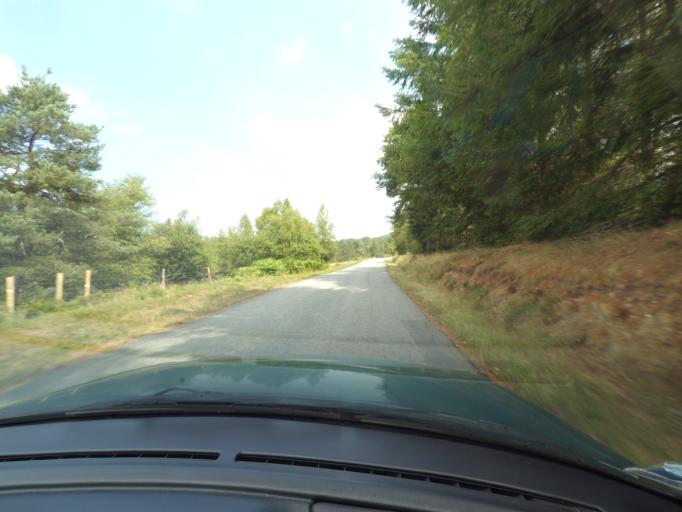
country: FR
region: Limousin
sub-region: Departement de la Correze
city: Bugeat
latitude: 45.7323
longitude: 1.9915
